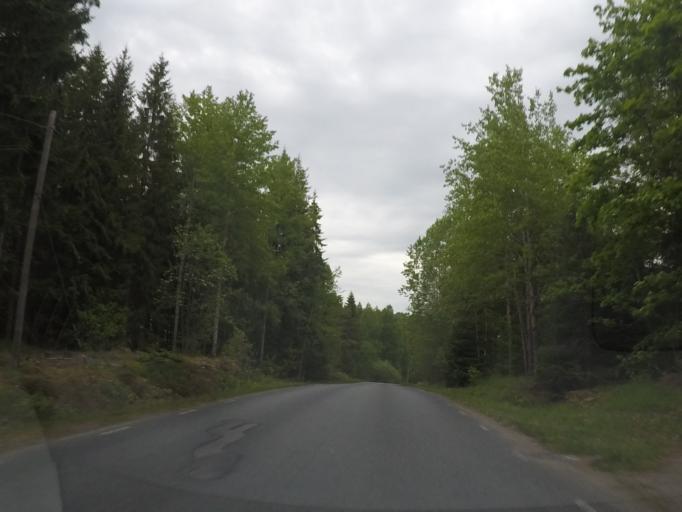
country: SE
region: Soedermanland
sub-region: Eskilstuna Kommun
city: Arla
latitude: 59.2616
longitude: 16.6547
